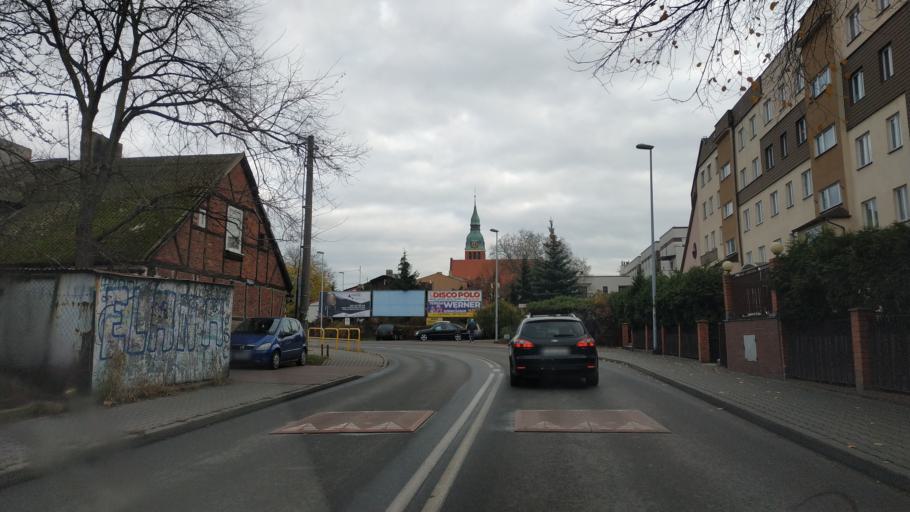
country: PL
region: Kujawsko-Pomorskie
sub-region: Torun
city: Torun
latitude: 53.0223
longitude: 18.6071
